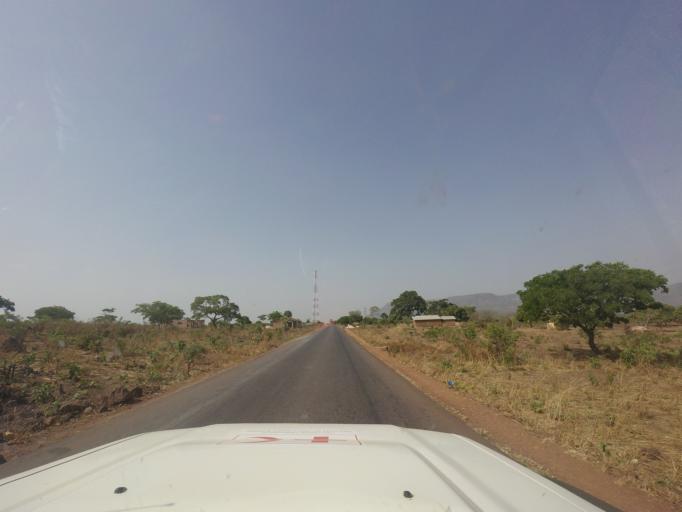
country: GN
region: Mamou
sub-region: Mamou Prefecture
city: Mamou
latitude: 10.2612
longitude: -12.4549
